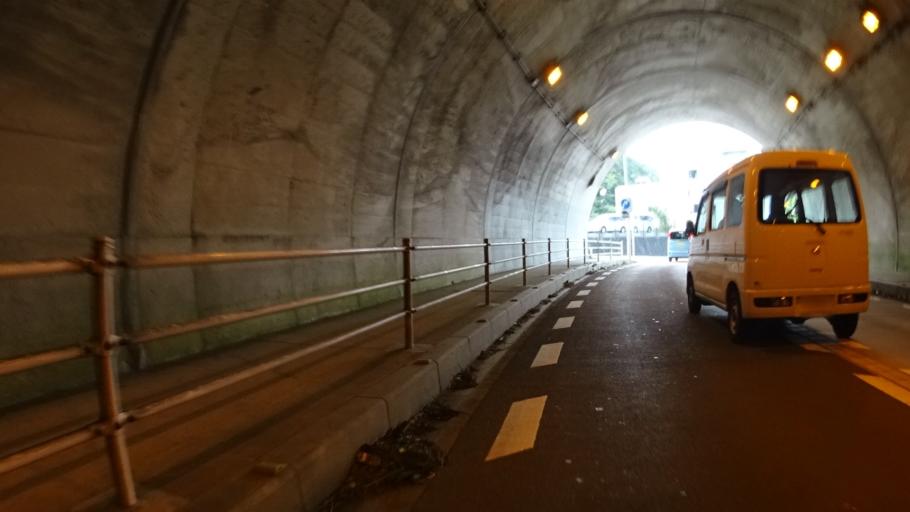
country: JP
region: Kanagawa
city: Yokosuka
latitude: 35.2307
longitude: 139.7231
